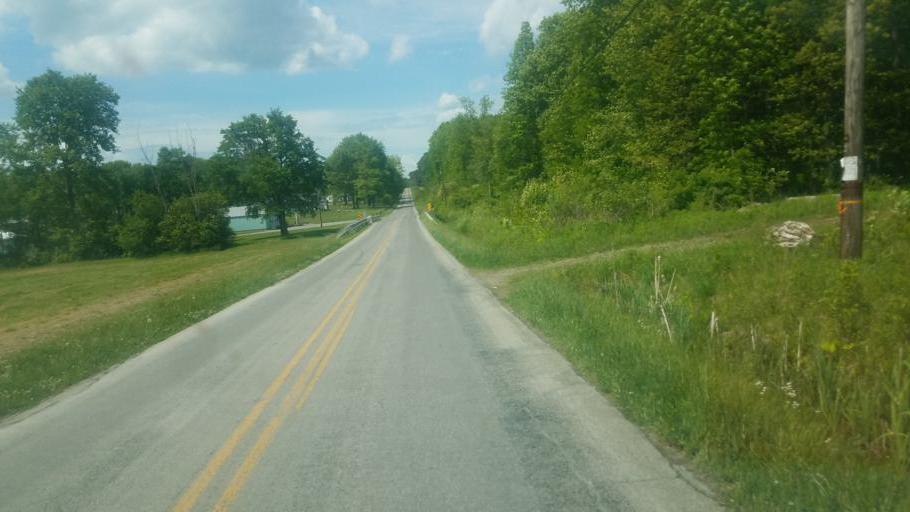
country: US
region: Pennsylvania
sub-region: Venango County
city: Franklin
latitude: 41.2193
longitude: -79.8456
